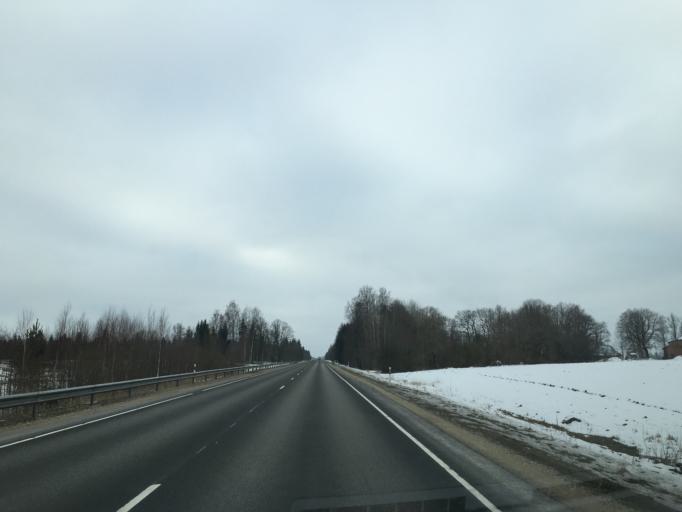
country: EE
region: Tartu
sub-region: Elva linn
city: Elva
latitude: 58.2135
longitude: 26.3633
